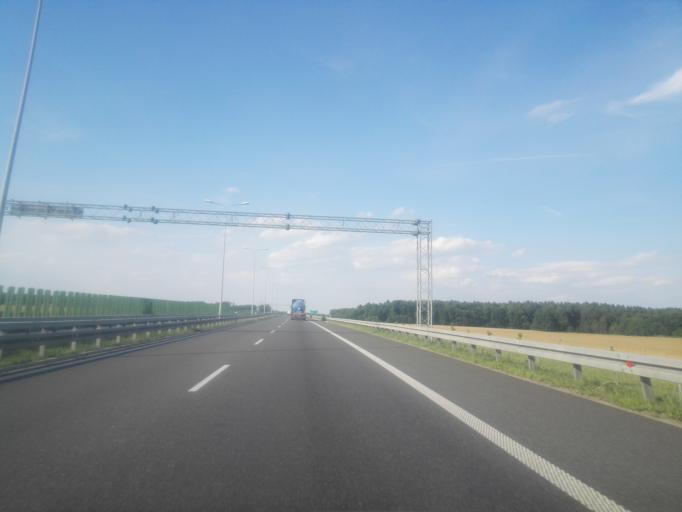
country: PL
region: Lower Silesian Voivodeship
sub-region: Powiat olesnicki
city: Twardogora
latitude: 51.2877
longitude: 17.5765
